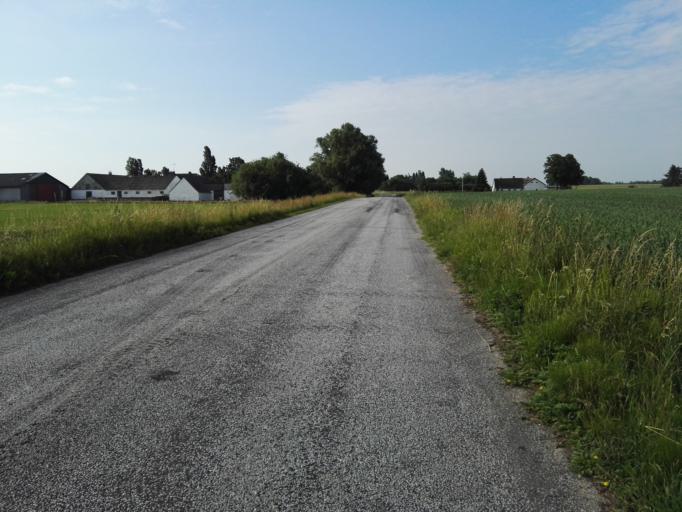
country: DK
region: Capital Region
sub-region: Egedal Kommune
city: Olstykke
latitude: 55.8072
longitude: 12.1090
